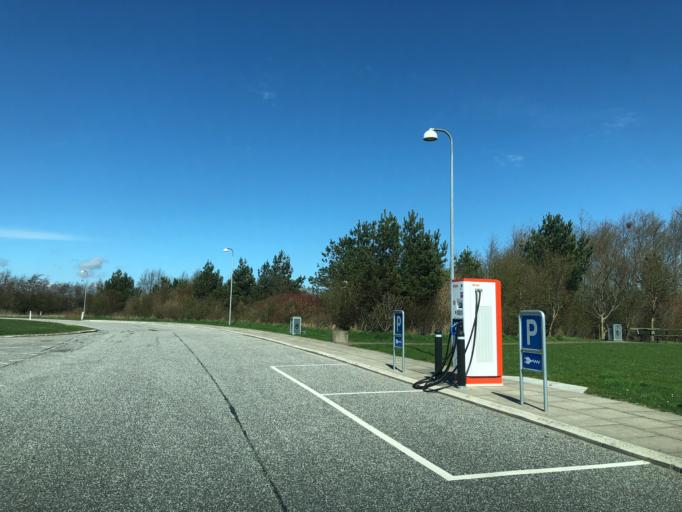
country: DK
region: North Denmark
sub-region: Bronderslev Kommune
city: Bronderslev
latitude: 57.2216
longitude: 9.9419
